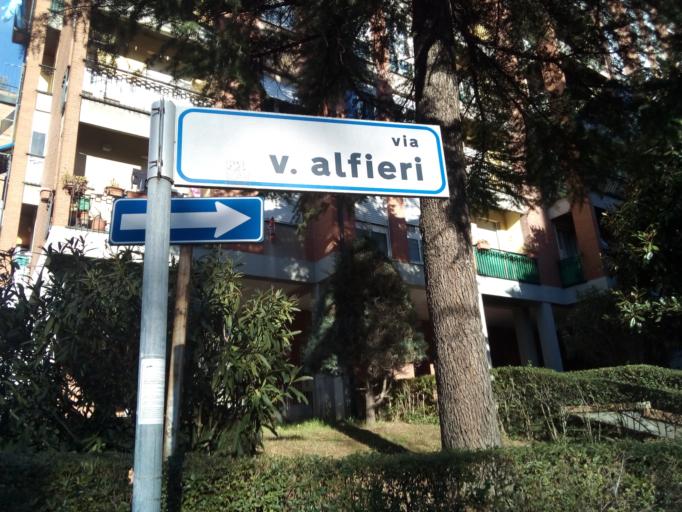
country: IT
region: Umbria
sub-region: Provincia di Perugia
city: Perugia
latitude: 43.0950
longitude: 12.3909
